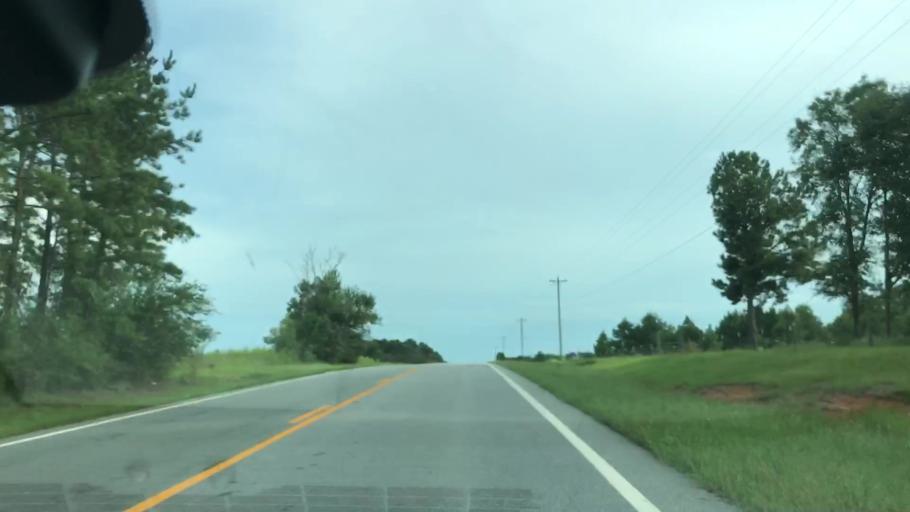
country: US
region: Georgia
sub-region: Quitman County
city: Georgetown
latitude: 31.7891
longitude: -85.0920
